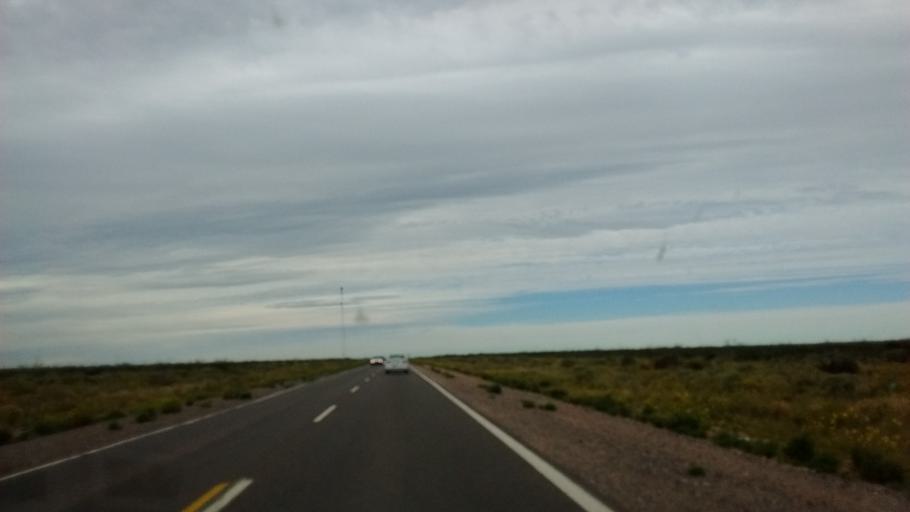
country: AR
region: Rio Negro
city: Contraalmirante Cordero
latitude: -38.3155
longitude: -68.0046
